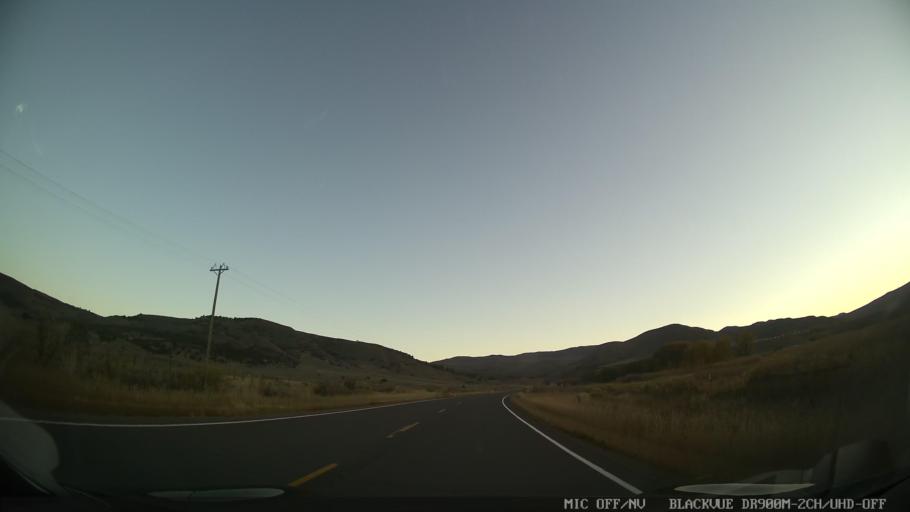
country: US
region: Colorado
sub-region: Eagle County
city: Edwards
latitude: 39.7425
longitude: -106.6777
